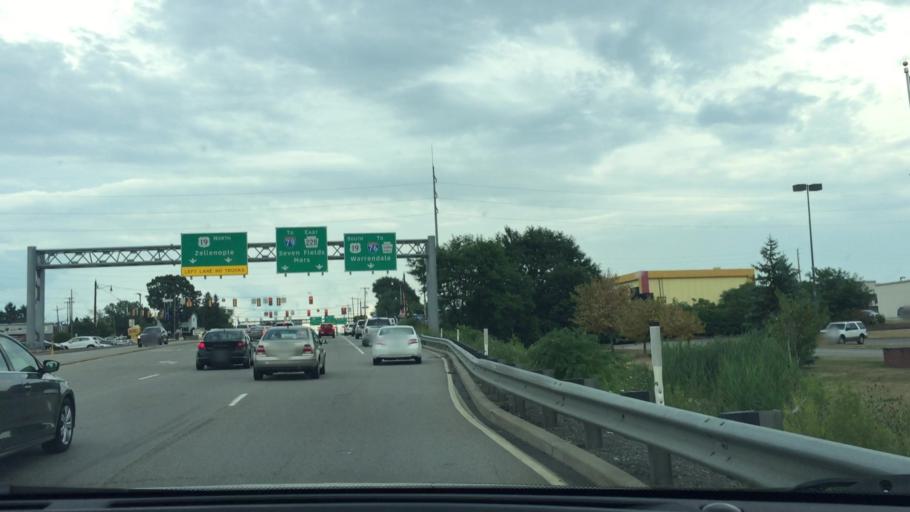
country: US
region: Pennsylvania
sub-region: Butler County
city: Cranberry Township
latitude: 40.6846
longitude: -80.1034
